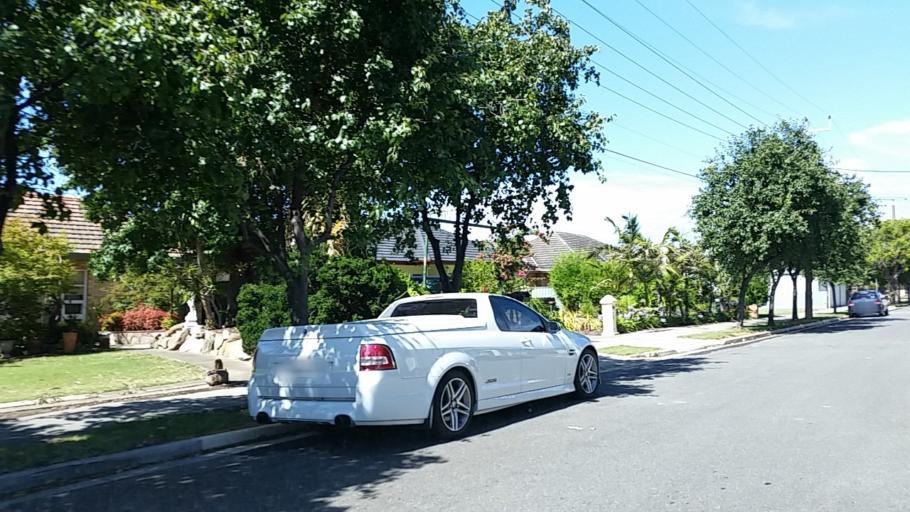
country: AU
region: South Australia
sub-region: Charles Sturt
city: Findon
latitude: -34.9228
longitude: 138.5276
